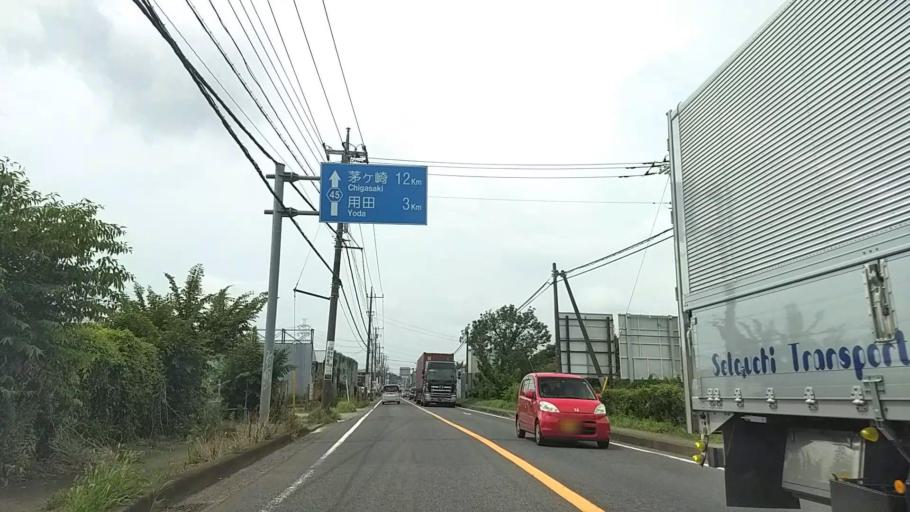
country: JP
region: Kanagawa
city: Minami-rinkan
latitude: 35.4275
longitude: 139.4318
